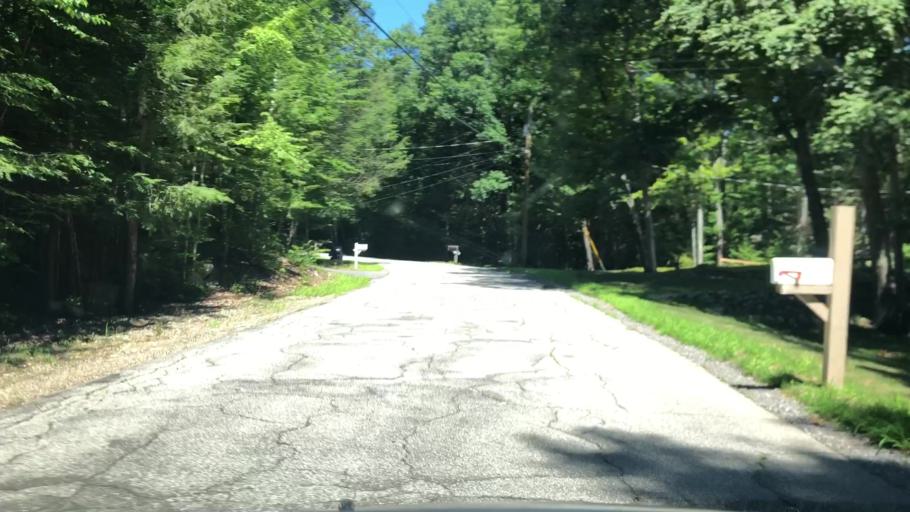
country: US
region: New Hampshire
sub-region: Hillsborough County
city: Mont Vernon
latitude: 42.9010
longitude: -71.6079
